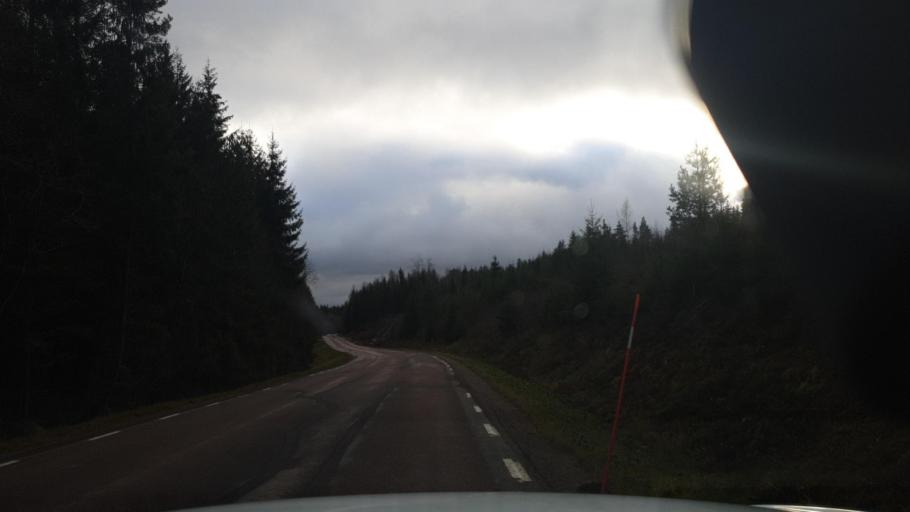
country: SE
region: Vaermland
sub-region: Arvika Kommun
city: Arvika
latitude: 59.6978
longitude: 12.7918
